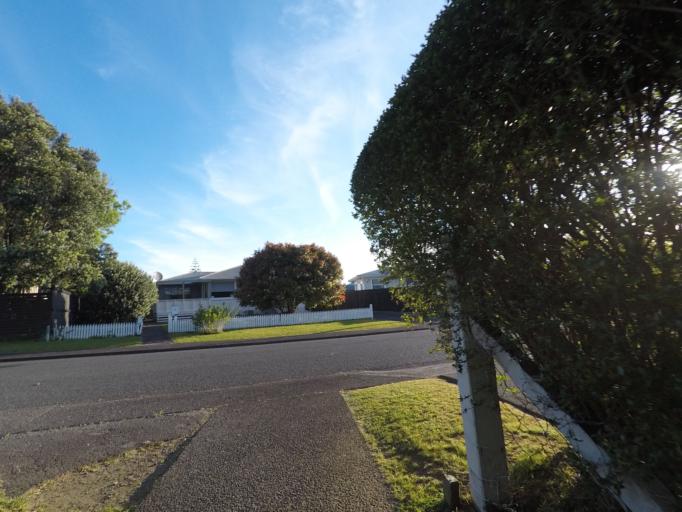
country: NZ
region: Auckland
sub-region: Auckland
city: Rosebank
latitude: -36.8451
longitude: 174.6497
